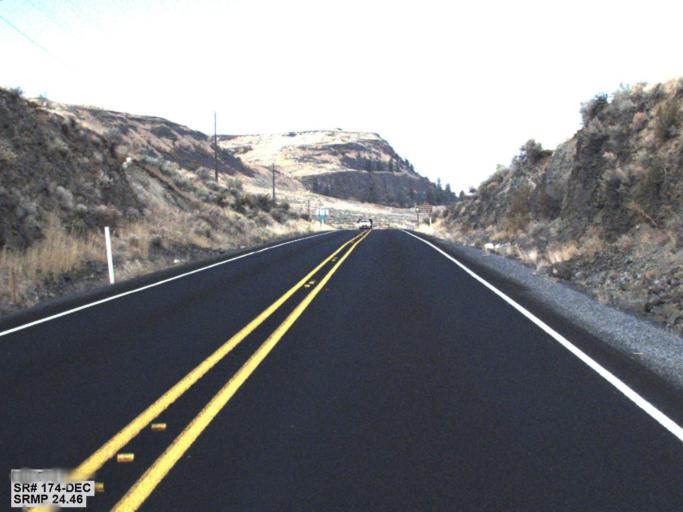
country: US
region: Washington
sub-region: Okanogan County
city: Coulee Dam
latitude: 47.9241
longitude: -118.9531
